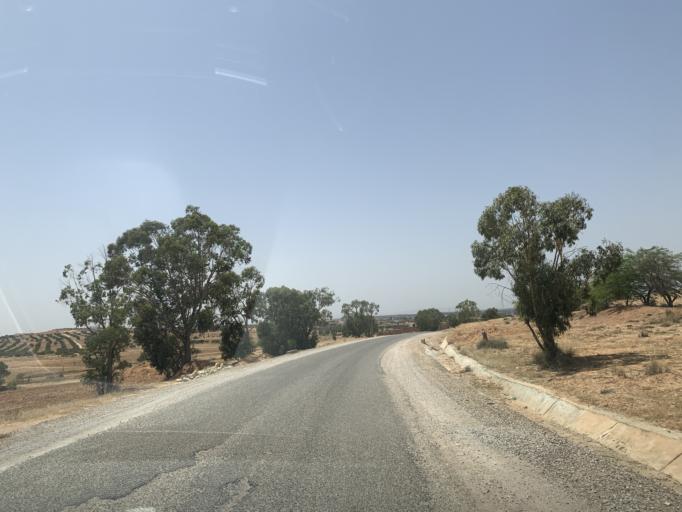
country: TN
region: Al Mahdiyah
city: Shurban
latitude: 35.1609
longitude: 10.2498
